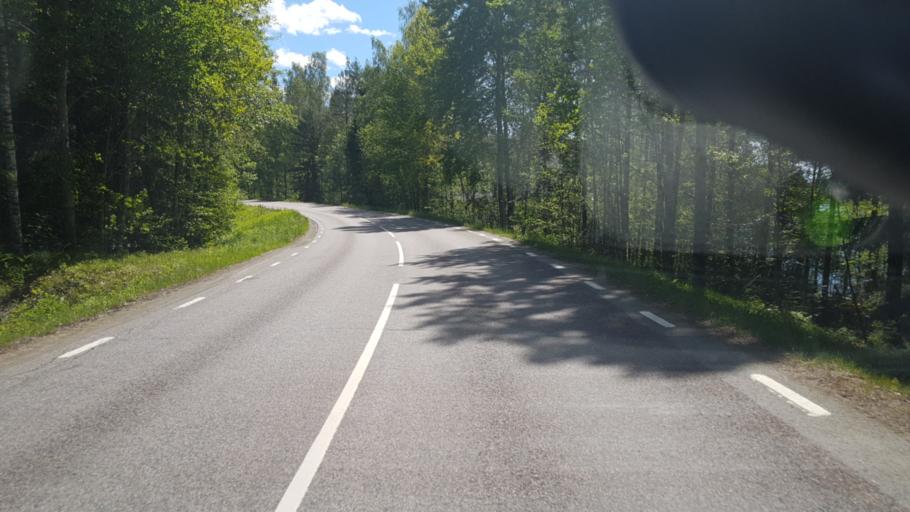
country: SE
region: Vaermland
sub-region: Grums Kommun
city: Slottsbron
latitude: 59.4504
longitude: 12.8973
